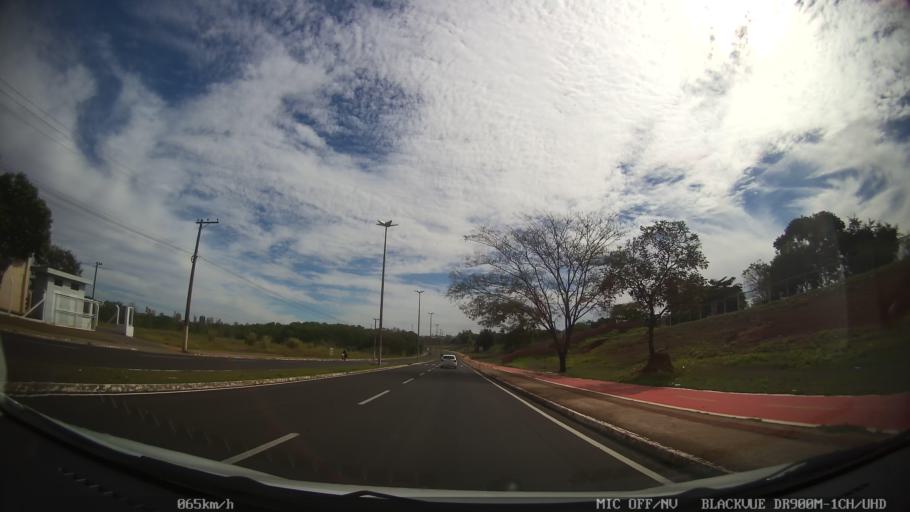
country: BR
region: Sao Paulo
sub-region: Catanduva
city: Catanduva
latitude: -21.1454
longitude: -48.9506
